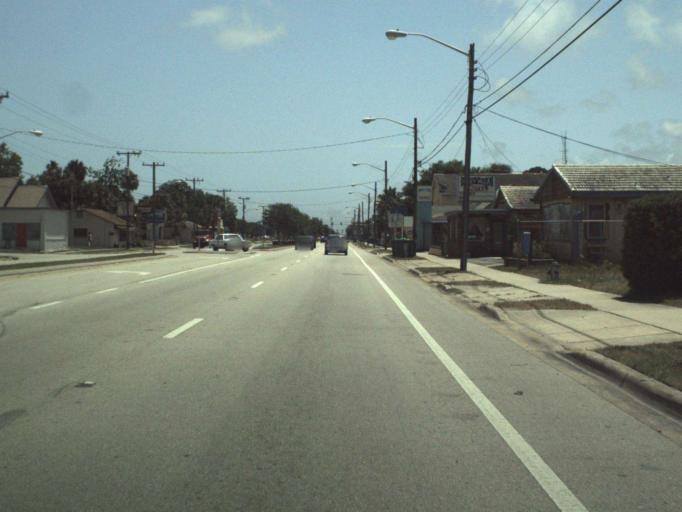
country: US
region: Florida
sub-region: Volusia County
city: Holly Hill
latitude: 29.2347
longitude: -81.0358
